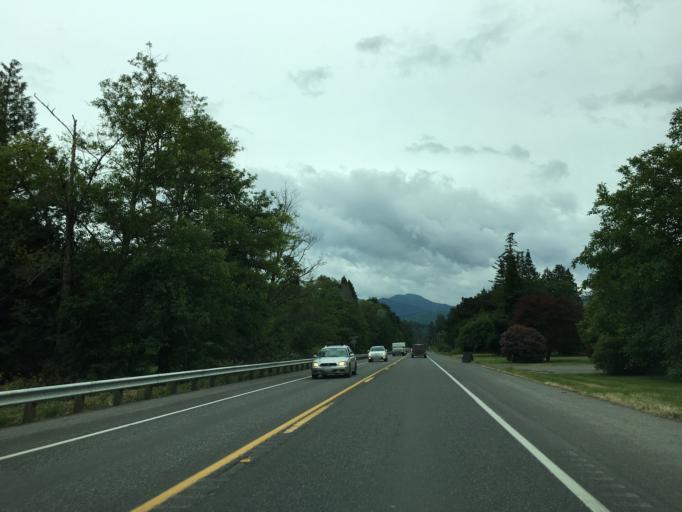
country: US
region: Washington
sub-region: Whatcom County
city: Nooksack
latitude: 48.8317
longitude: -122.2388
